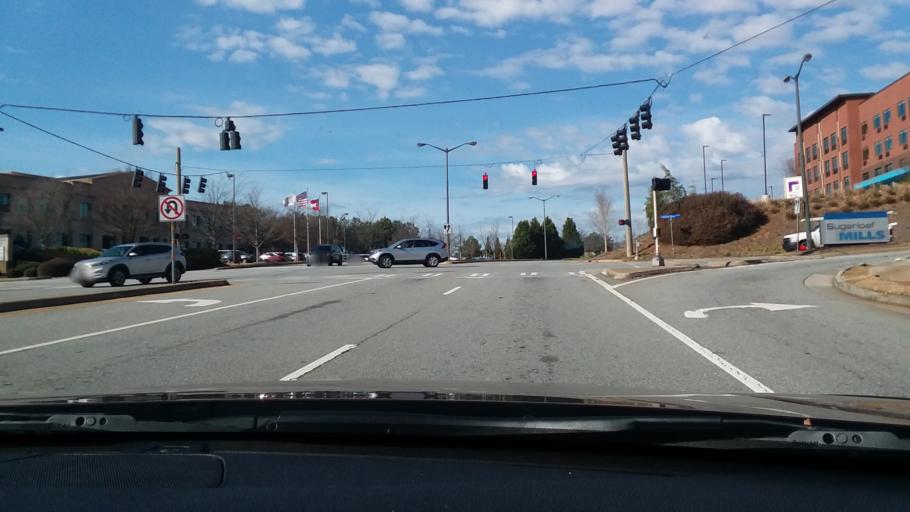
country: US
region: Georgia
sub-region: Gwinnett County
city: Duluth
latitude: 33.9789
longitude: -84.0846
